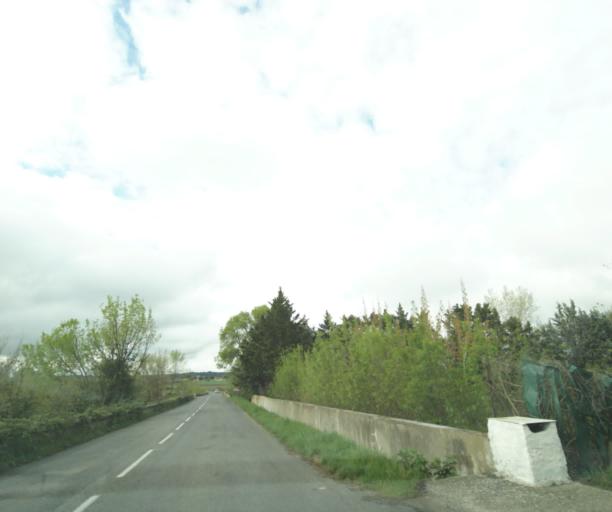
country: FR
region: Languedoc-Roussillon
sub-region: Departement de l'Herault
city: Saussan
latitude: 43.5740
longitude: 3.7718
